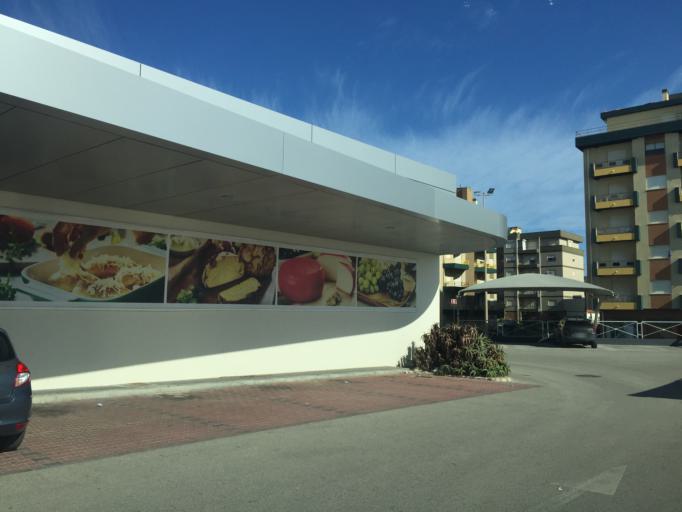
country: PT
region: Coimbra
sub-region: Figueira da Foz
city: Buarcos
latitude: 40.1673
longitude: -8.8837
